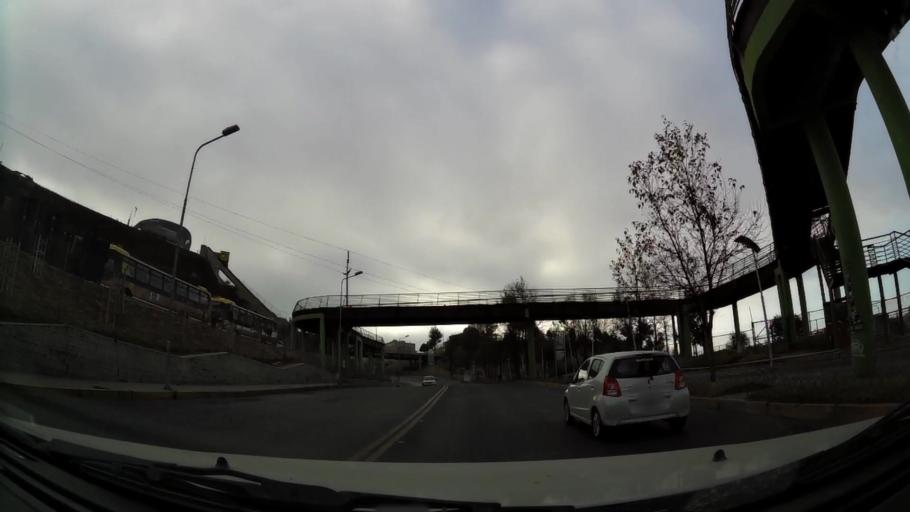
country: BO
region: La Paz
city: La Paz
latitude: -16.5024
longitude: -68.1261
